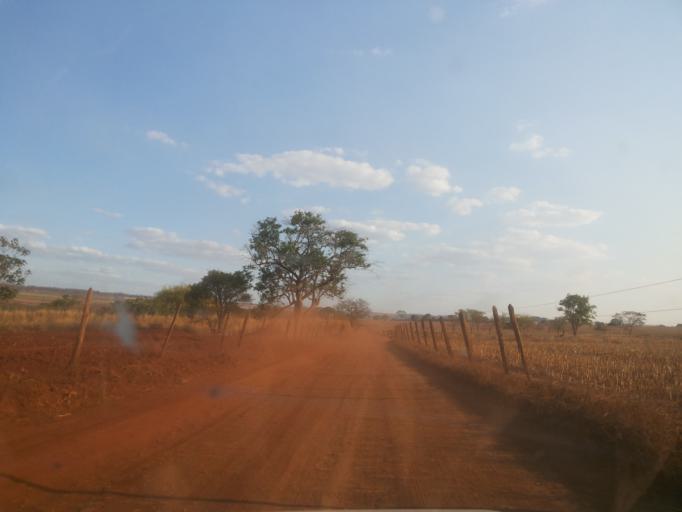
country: BR
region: Minas Gerais
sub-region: Capinopolis
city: Capinopolis
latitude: -18.6898
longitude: -49.3764
